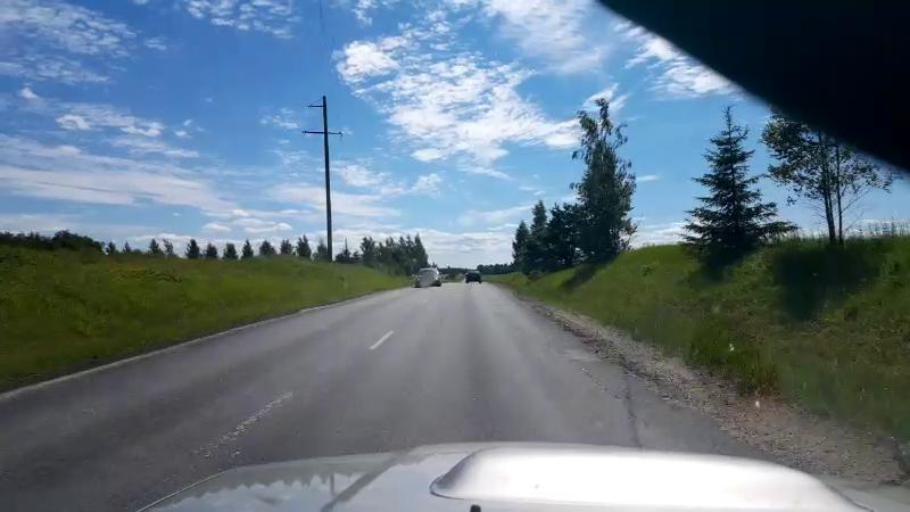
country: EE
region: Jogevamaa
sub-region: Jogeva linn
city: Jogeva
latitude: 58.8386
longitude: 26.2902
